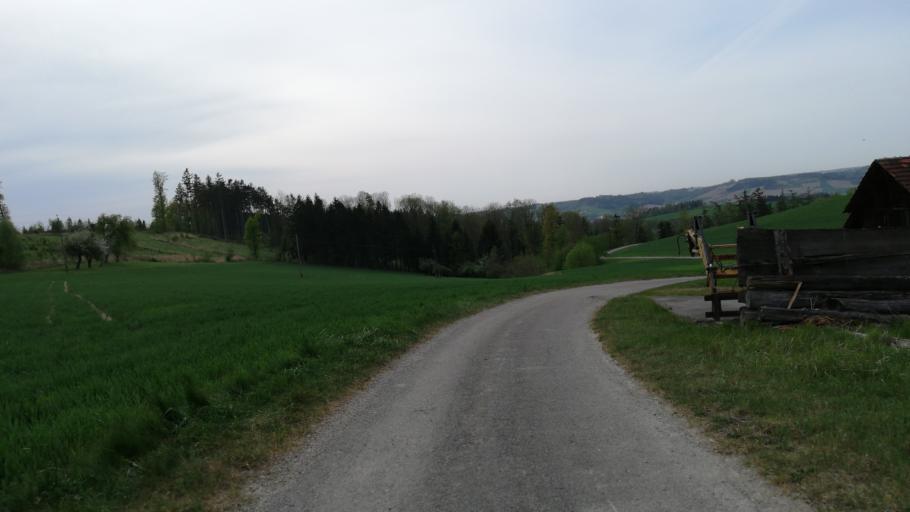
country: AT
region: Upper Austria
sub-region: Wels-Land
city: Gunskirchen
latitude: 48.1825
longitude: 13.9580
